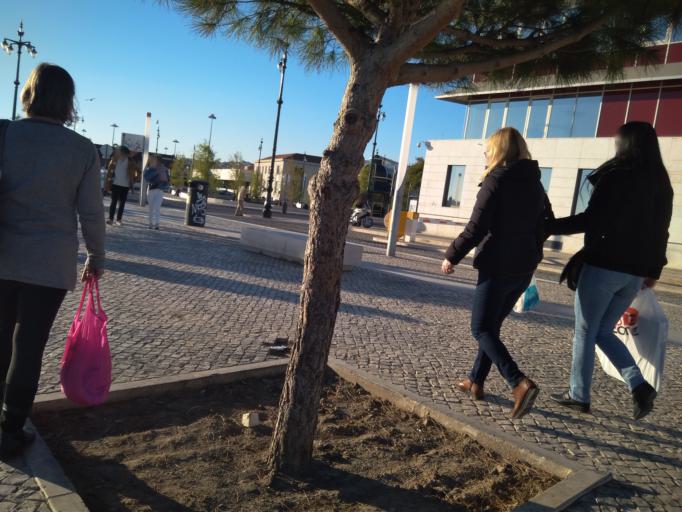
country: PT
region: Lisbon
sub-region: Lisbon
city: Lisbon
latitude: 38.7053
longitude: -9.1428
